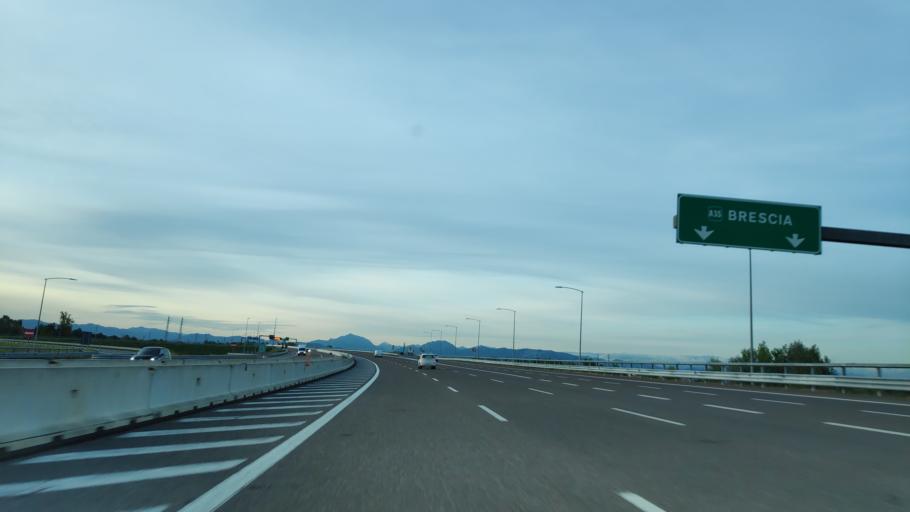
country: IT
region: Lombardy
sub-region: Citta metropolitana di Milano
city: Pozzuolo Martesana
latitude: 45.4986
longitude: 9.4451
